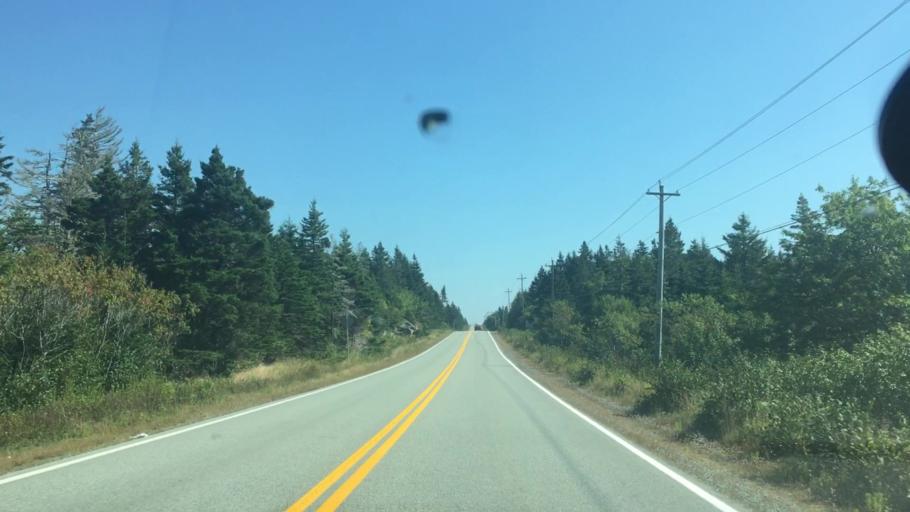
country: CA
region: Nova Scotia
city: New Glasgow
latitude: 44.9312
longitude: -62.2936
